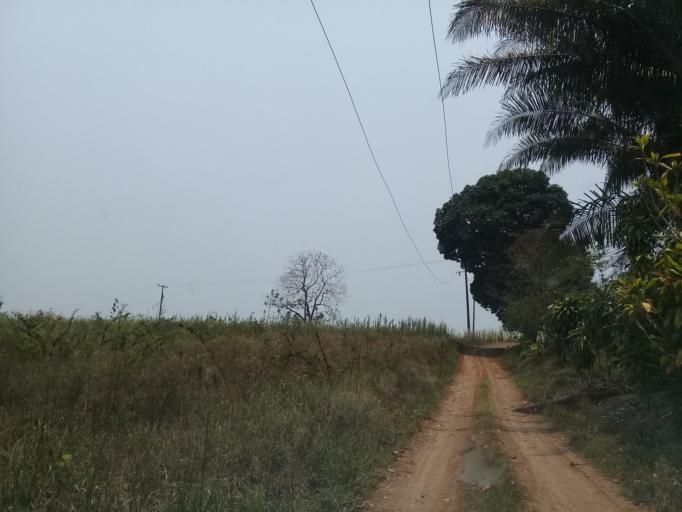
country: MX
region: Veracruz
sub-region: Tezonapa
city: Laguna Chica (Pueblo Nuevo)
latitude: 18.5382
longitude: -96.7316
